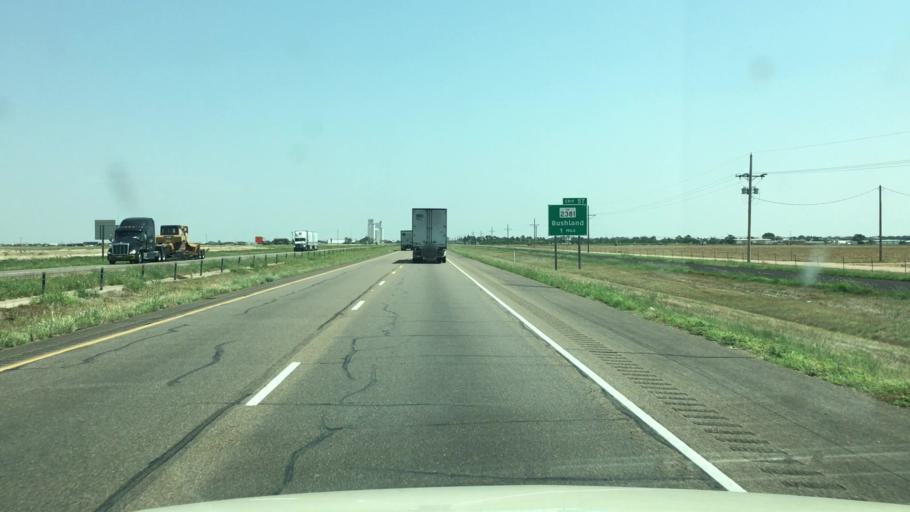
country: US
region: Texas
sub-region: Potter County
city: Bushland
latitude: 35.1918
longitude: -102.0887
